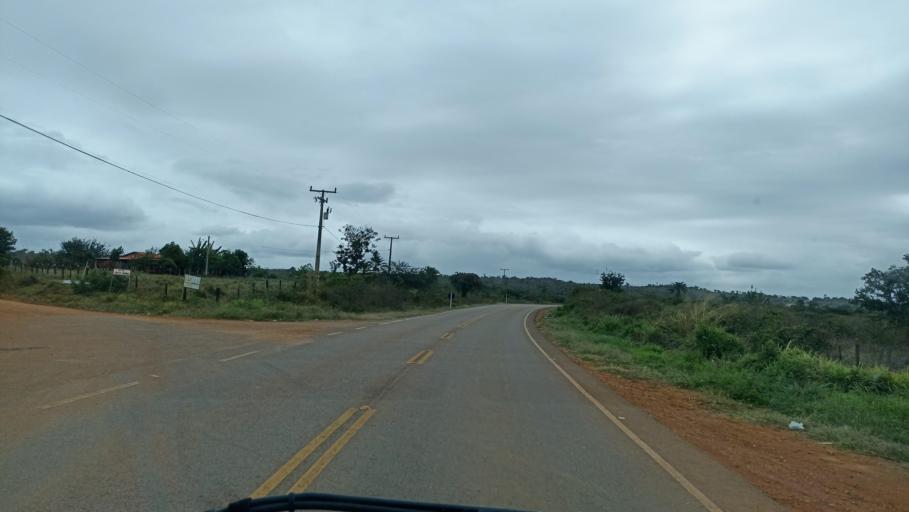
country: BR
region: Bahia
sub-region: Andarai
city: Vera Cruz
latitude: -13.0044
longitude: -40.9850
